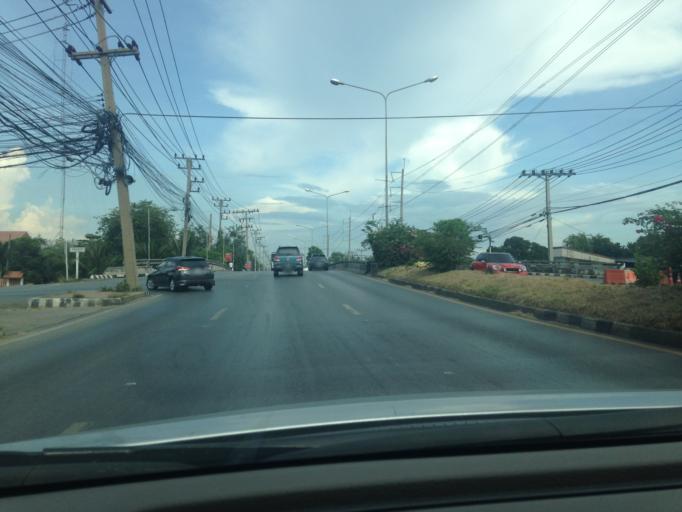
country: TH
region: Pathum Thani
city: Khlong Luang
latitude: 14.0660
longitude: 100.6629
